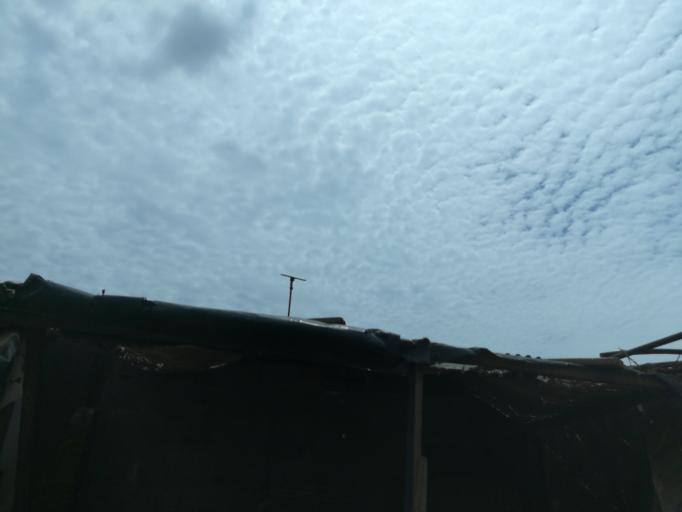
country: NG
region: Lagos
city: Oshodi
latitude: 6.5614
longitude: 3.3303
